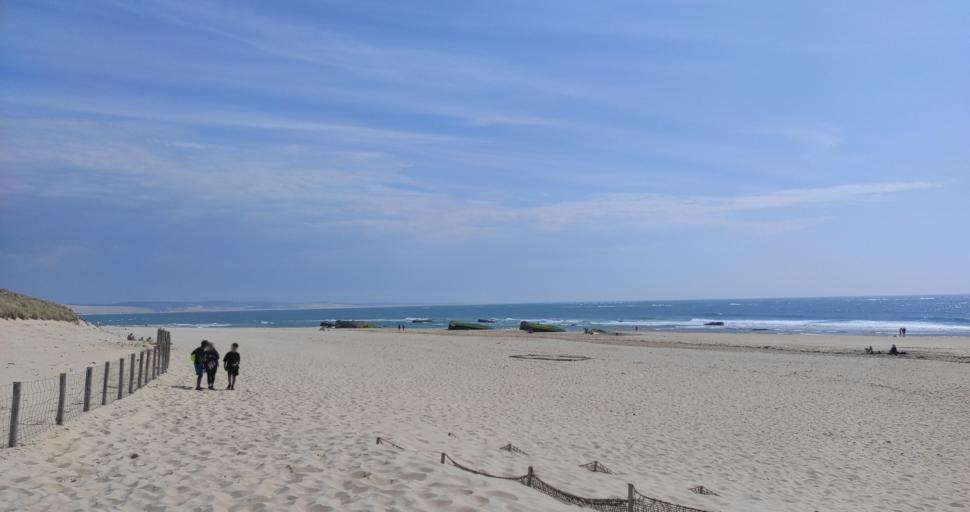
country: FR
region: Aquitaine
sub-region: Departement de la Gironde
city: Arcachon
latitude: 44.6263
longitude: -1.2571
